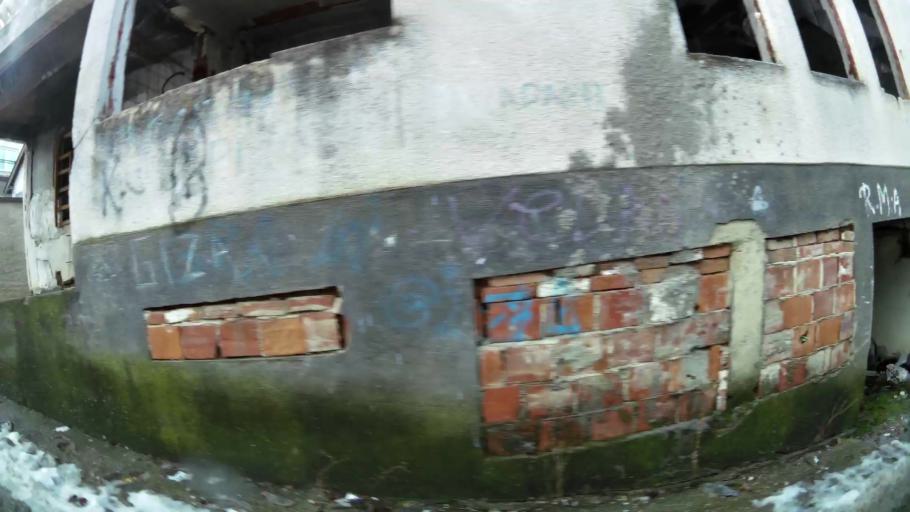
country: XK
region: Pristina
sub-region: Komuna e Prishtines
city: Pristina
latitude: 42.6619
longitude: 21.1732
